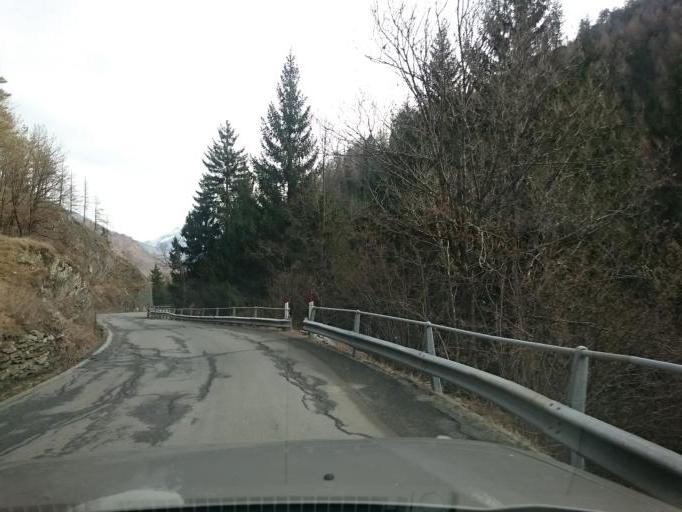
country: IT
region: Lombardy
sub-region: Provincia di Brescia
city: Corteno Golgi
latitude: 46.1624
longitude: 10.1999
